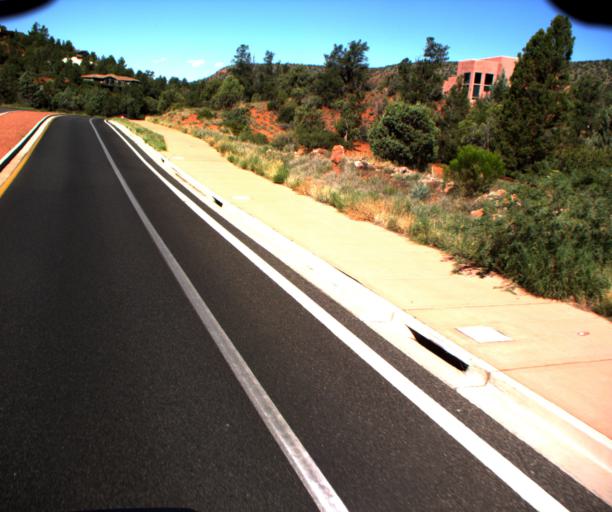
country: US
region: Arizona
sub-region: Coconino County
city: Sedona
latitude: 34.8443
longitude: -111.7696
